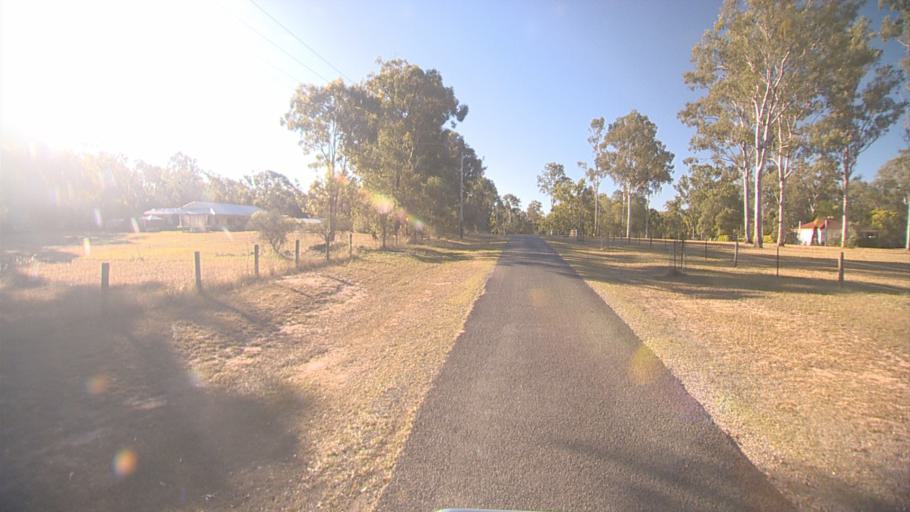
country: AU
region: Queensland
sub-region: Logan
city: North Maclean
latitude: -27.7553
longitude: 153.0096
